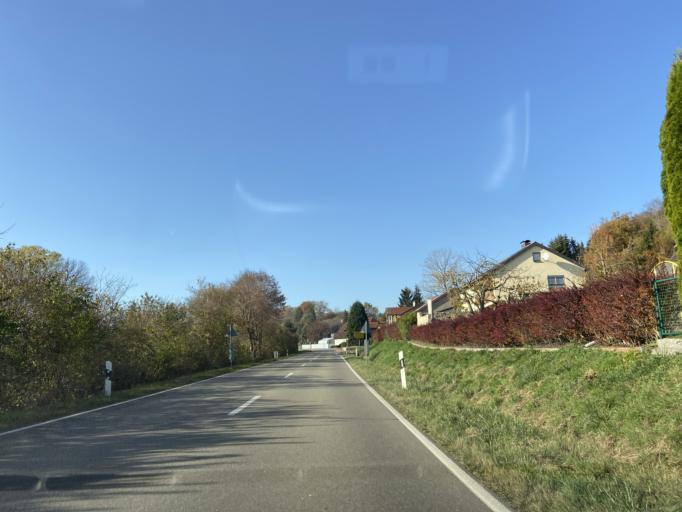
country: DE
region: Baden-Wuerttemberg
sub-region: Tuebingen Region
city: Krauchenwies
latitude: 48.0385
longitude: 9.2823
